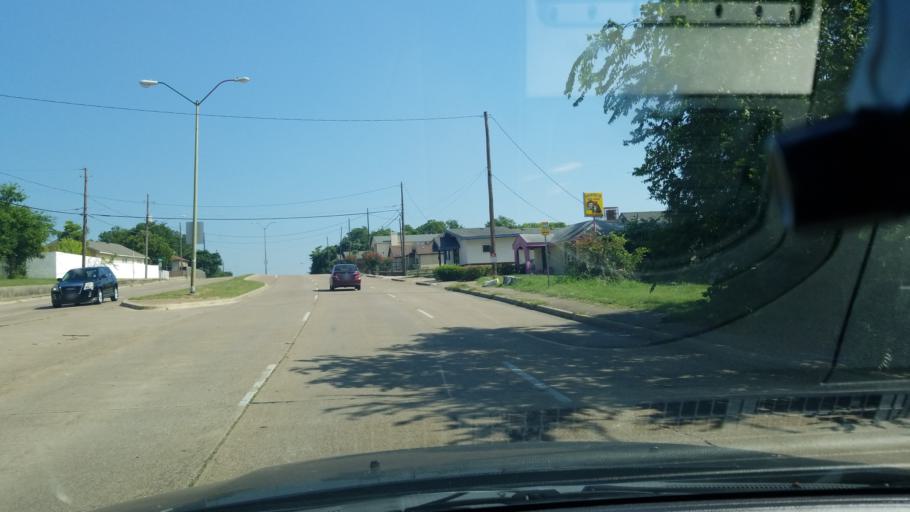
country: US
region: Texas
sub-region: Dallas County
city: Dallas
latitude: 32.7409
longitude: -96.7983
